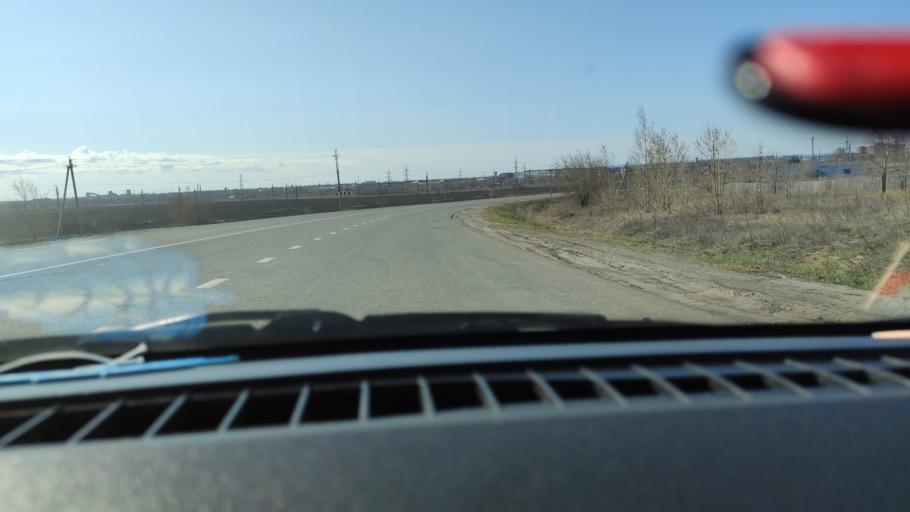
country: RU
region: Samara
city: Syzran'
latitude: 53.2021
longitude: 48.5093
